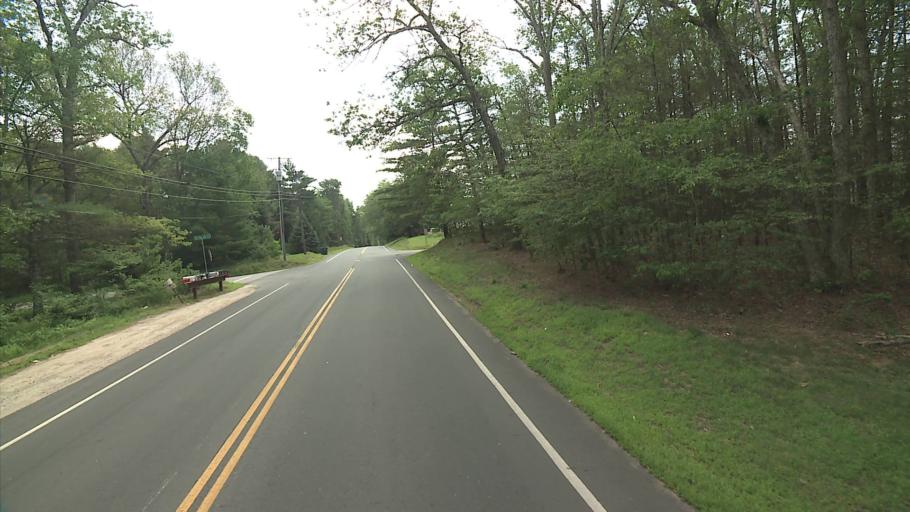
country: US
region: Connecticut
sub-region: New London County
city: Preston City
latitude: 41.5653
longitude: -71.8685
